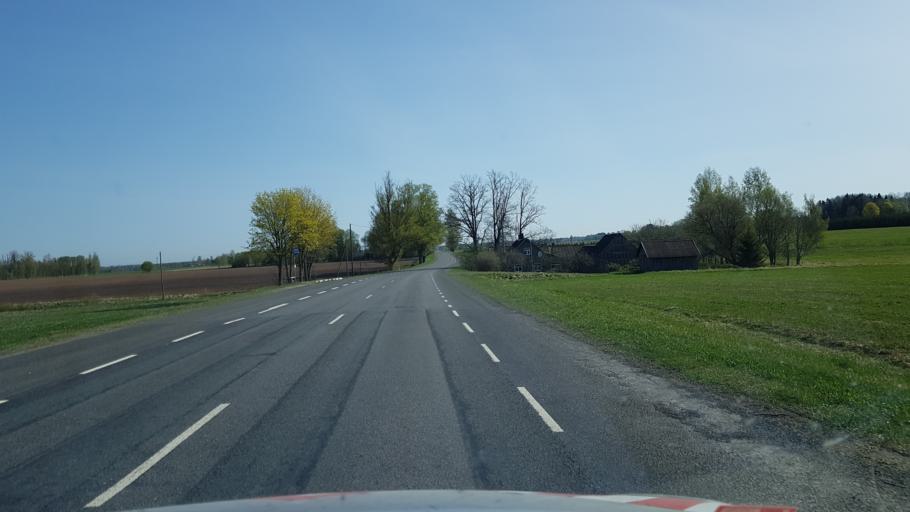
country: EE
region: Viljandimaa
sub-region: Karksi vald
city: Karksi-Nuia
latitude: 58.1690
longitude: 25.4707
